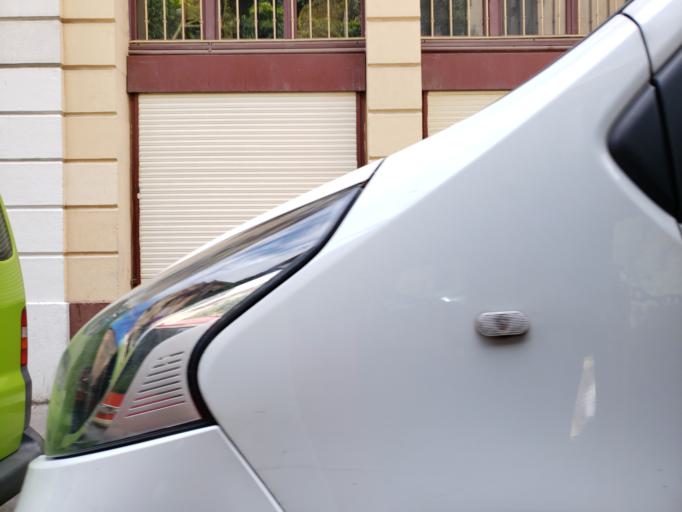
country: FR
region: Rhone-Alpes
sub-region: Departement du Rhone
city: Caluire-et-Cuire
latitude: 45.7729
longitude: 4.8322
